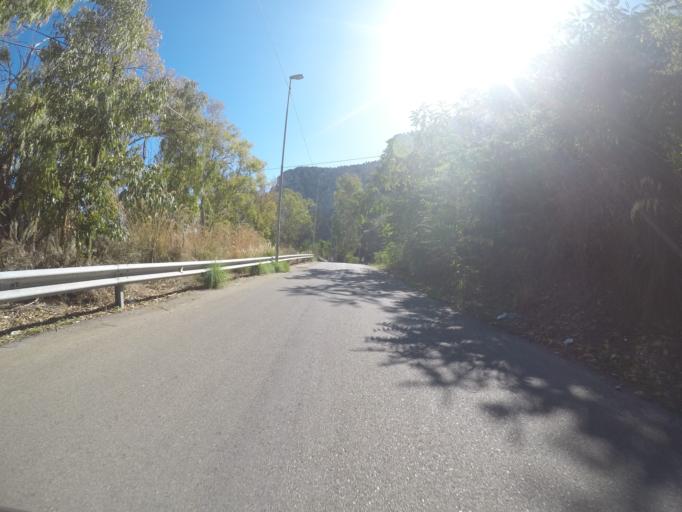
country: IT
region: Sicily
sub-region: Palermo
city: Palermo
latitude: 38.1886
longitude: 13.3425
